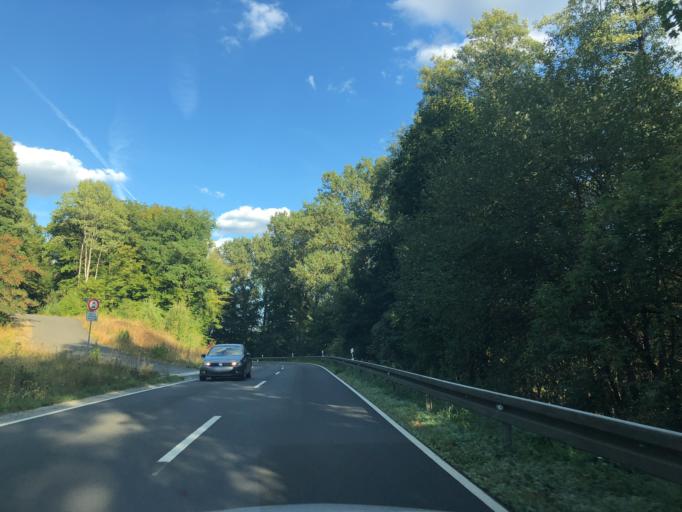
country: DE
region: Bavaria
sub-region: Upper Franconia
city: Burgwindheim
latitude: 49.8333
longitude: 10.5500
